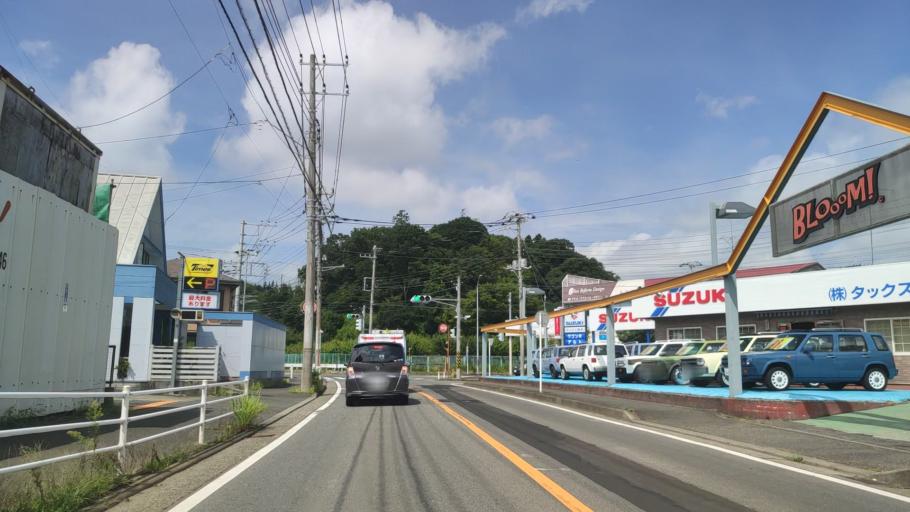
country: JP
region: Kanagawa
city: Minami-rinkan
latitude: 35.4303
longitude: 139.5391
